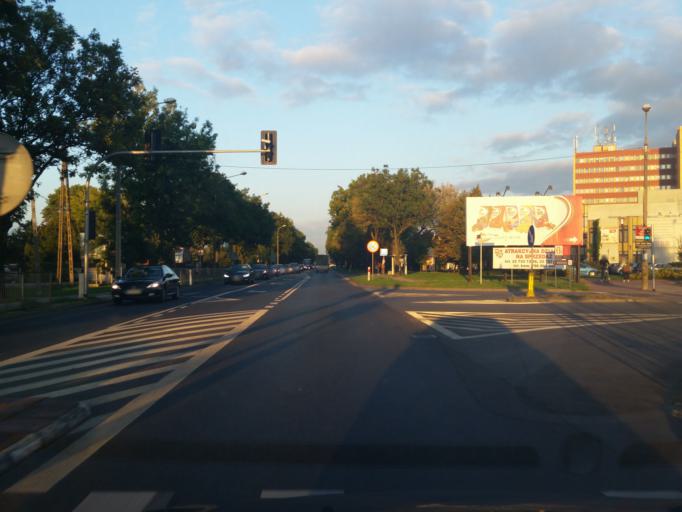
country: PL
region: Masovian Voivodeship
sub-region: Powiat warszawski zachodni
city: Ozarow Mazowiecki
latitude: 52.2111
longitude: 20.8172
